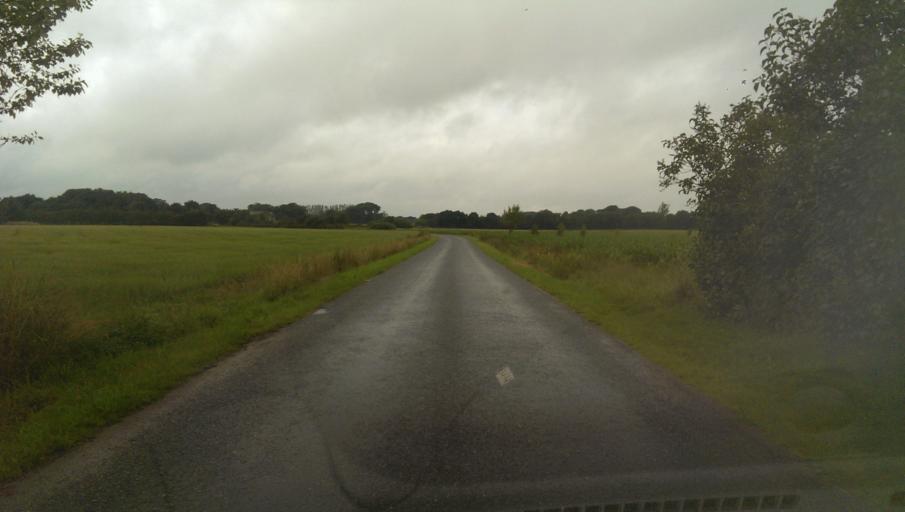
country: DK
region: South Denmark
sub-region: Esbjerg Kommune
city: Bramming
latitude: 55.4930
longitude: 8.6630
